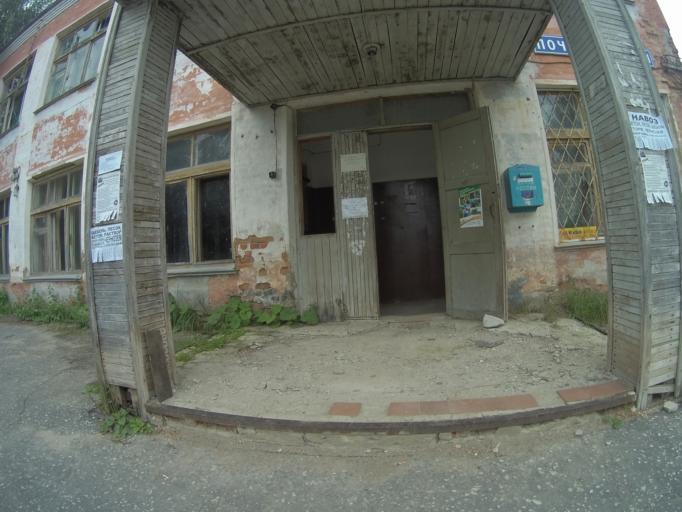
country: RU
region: Vladimir
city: Raduzhnyy
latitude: 55.9975
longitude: 40.2103
